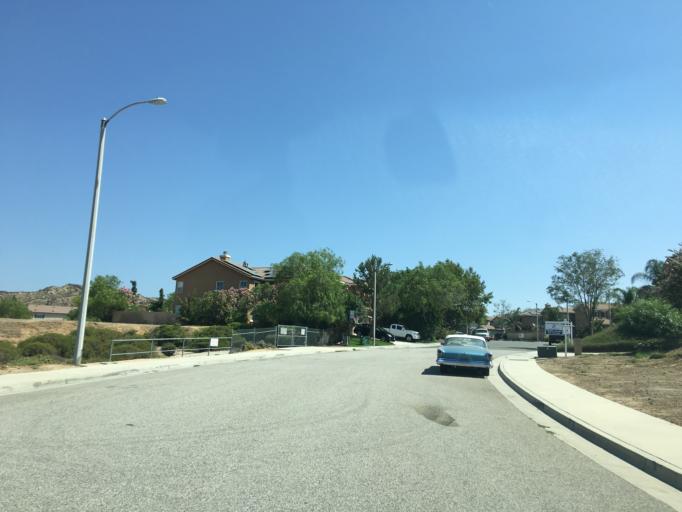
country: US
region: California
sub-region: Los Angeles County
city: Val Verde
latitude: 34.4680
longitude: -118.6425
